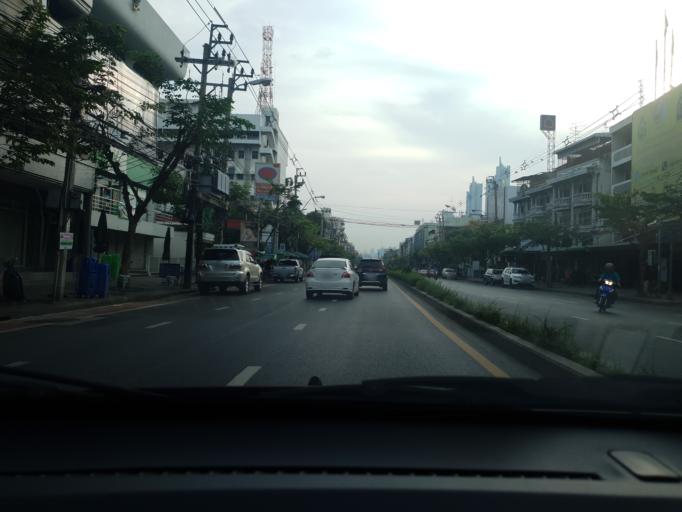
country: TH
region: Bangkok
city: Thon Buri
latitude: 13.7272
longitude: 100.4967
